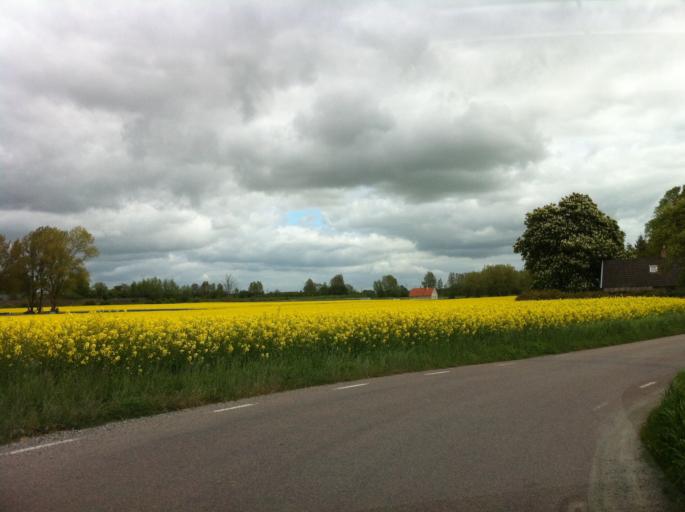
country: SE
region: Skane
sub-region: Kavlinge Kommun
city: Kaevlinge
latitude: 55.8137
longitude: 13.0600
